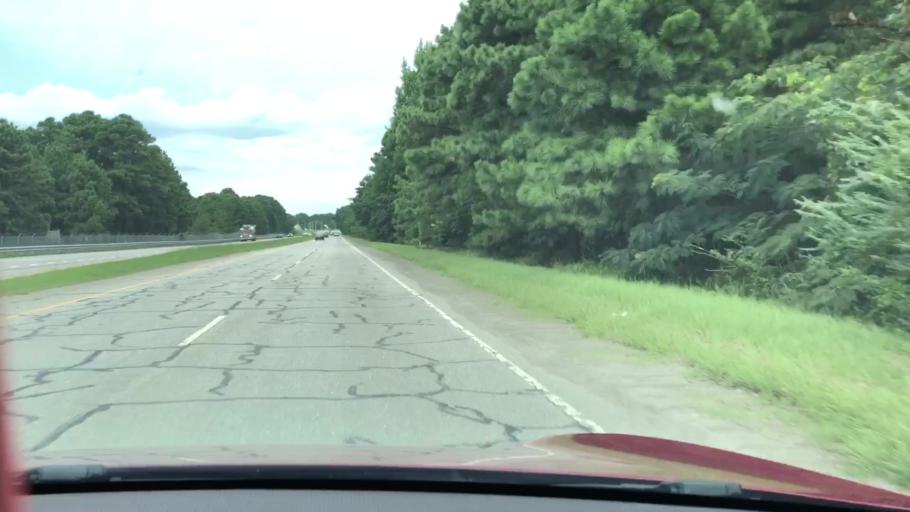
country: US
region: Virginia
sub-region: City of Virginia Beach
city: Virginia Beach
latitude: 36.8287
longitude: -76.0104
